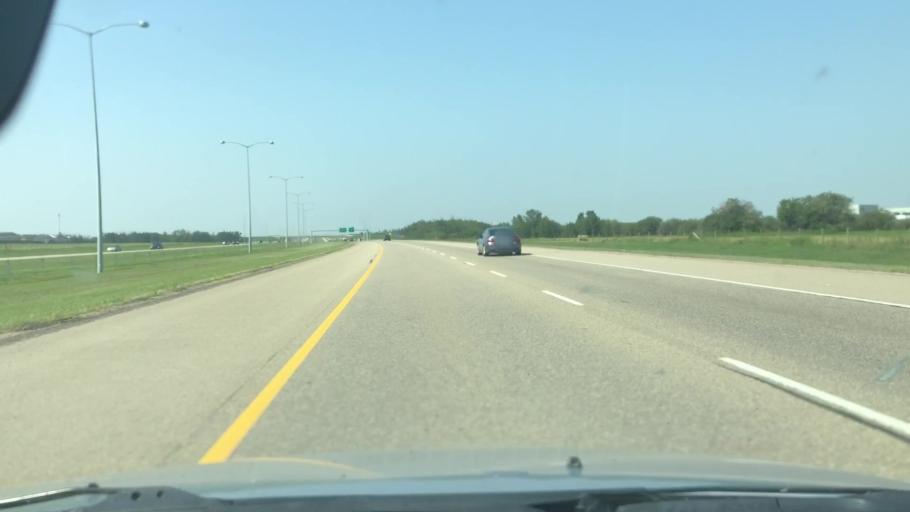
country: CA
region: Alberta
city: St. Albert
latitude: 53.6449
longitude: -113.5268
